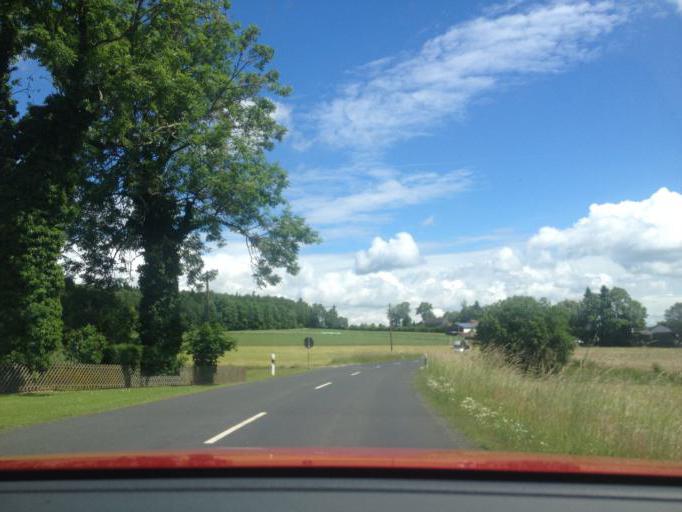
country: DE
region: Bavaria
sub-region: Upper Palatinate
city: Pechbrunn
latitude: 50.0034
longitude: 12.1936
